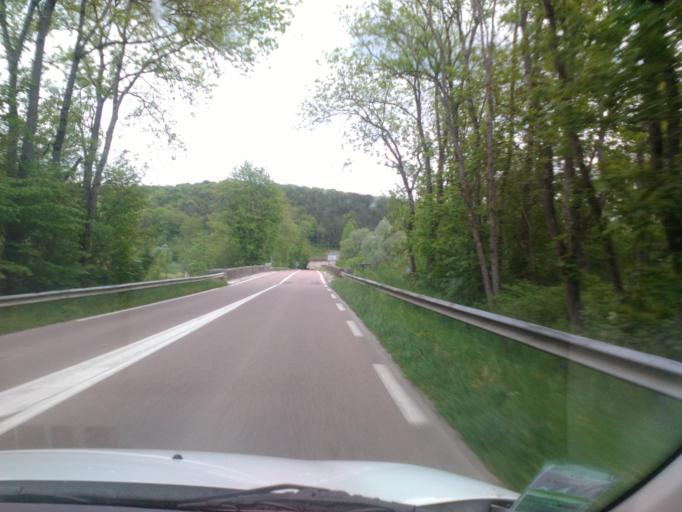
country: FR
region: Champagne-Ardenne
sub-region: Departement de l'Aube
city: Bar-sur-Aube
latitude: 48.2713
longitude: 4.6183
